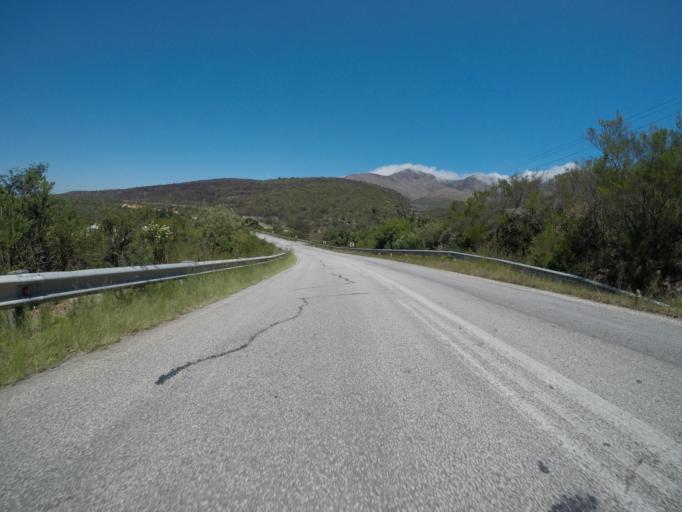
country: ZA
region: Eastern Cape
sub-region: Cacadu District Municipality
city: Kareedouw
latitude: -33.8932
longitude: 24.1024
